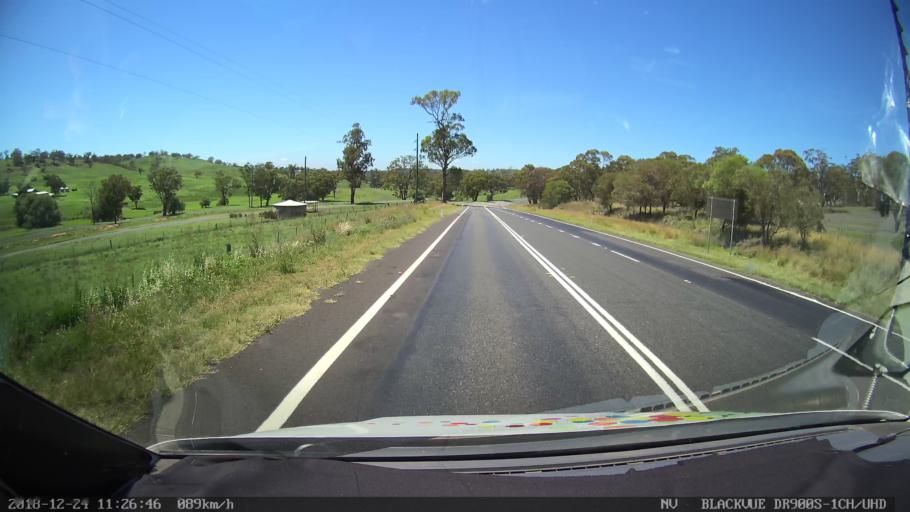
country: AU
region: New South Wales
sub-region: Upper Hunter Shire
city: Merriwa
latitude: -32.1732
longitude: 150.4332
